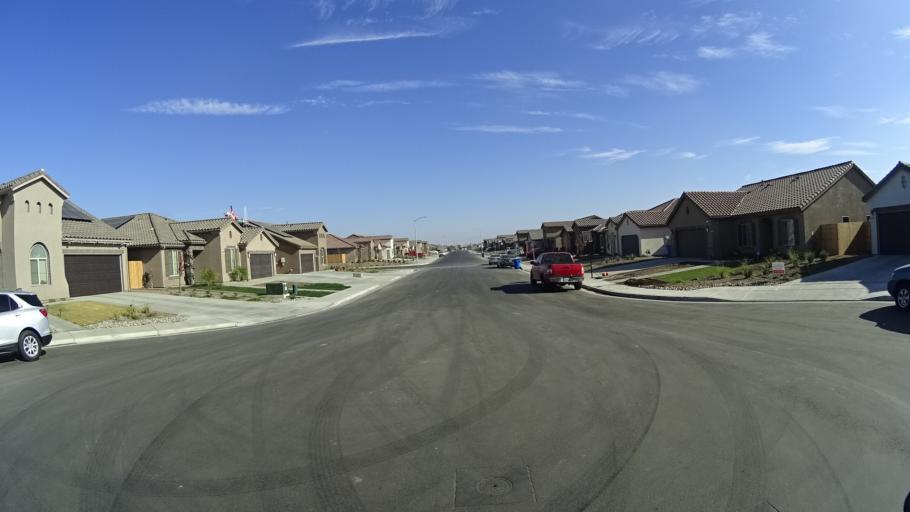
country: US
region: California
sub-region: Kern County
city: Greenfield
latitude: 35.2910
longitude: -119.0690
